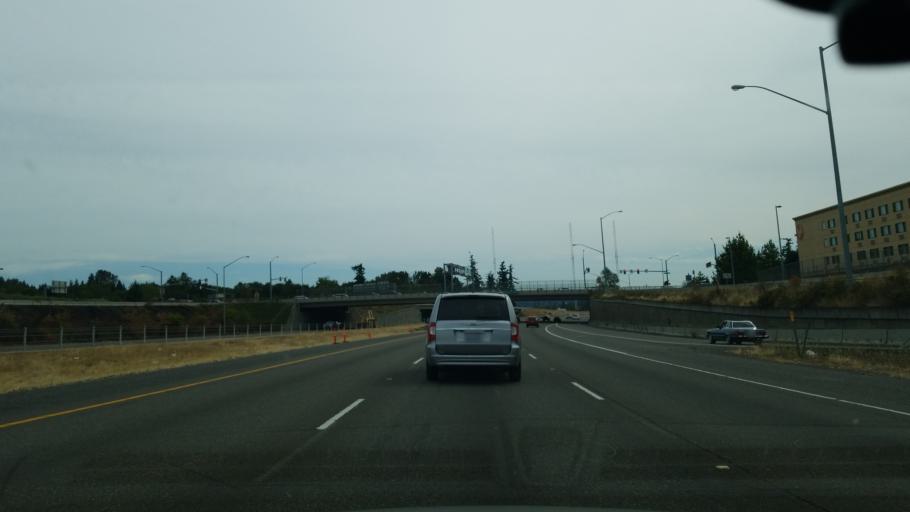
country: US
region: Oregon
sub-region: Clackamas County
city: Clackamas
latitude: 45.4312
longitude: -122.5660
